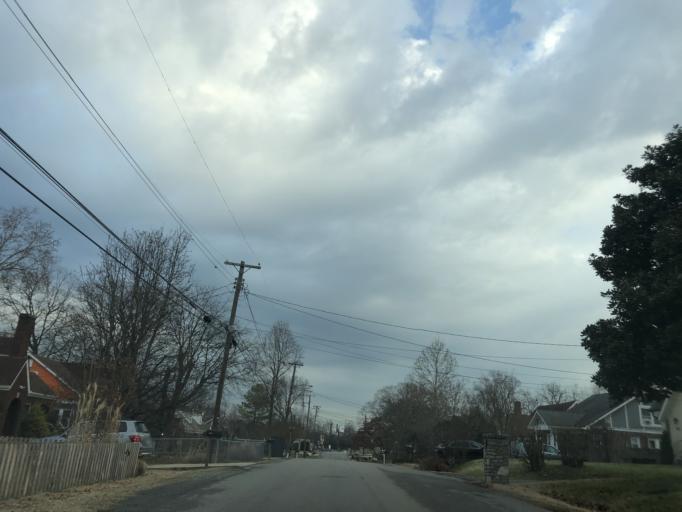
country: US
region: Tennessee
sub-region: Davidson County
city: Nashville
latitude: 36.2084
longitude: -86.7378
